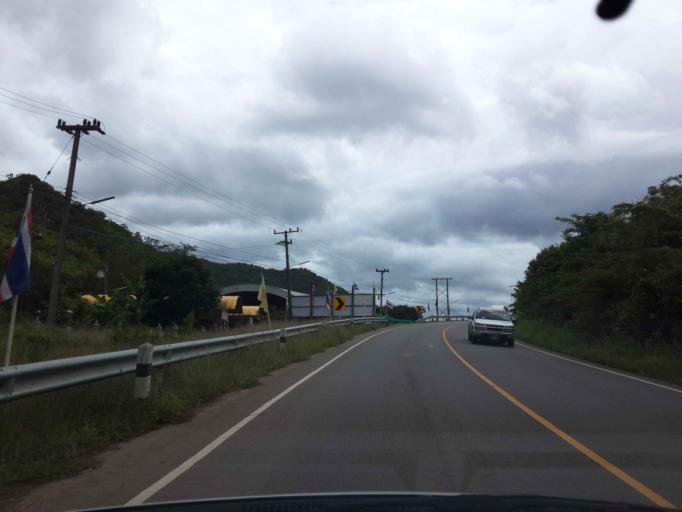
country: TH
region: Ratchaburi
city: Suan Phueng
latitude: 13.5670
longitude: 99.2618
